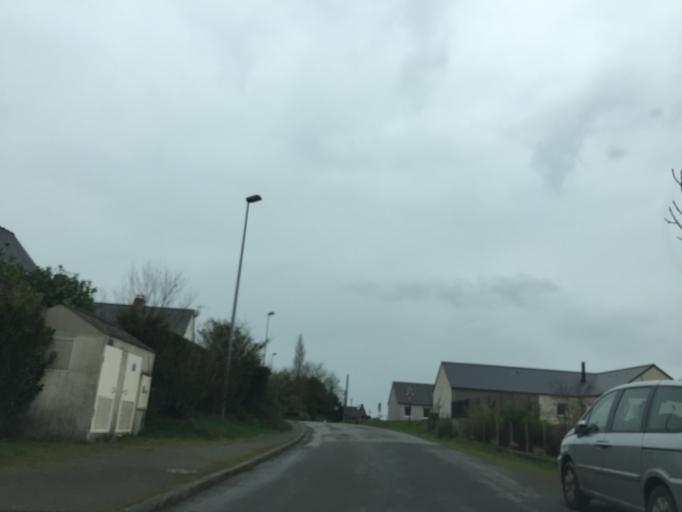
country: FR
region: Brittany
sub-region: Departement d'Ille-et-Vilaine
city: Lecousse
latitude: 48.3614
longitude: -1.2241
